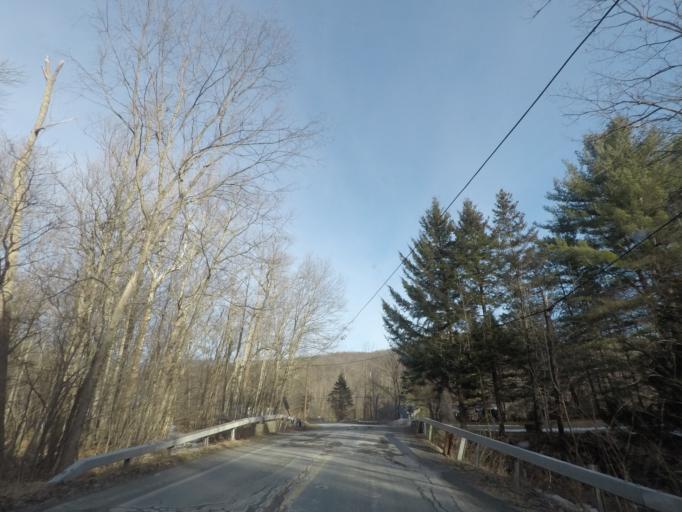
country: US
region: Massachusetts
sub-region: Berkshire County
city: Williamstown
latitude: 42.7361
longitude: -73.3637
